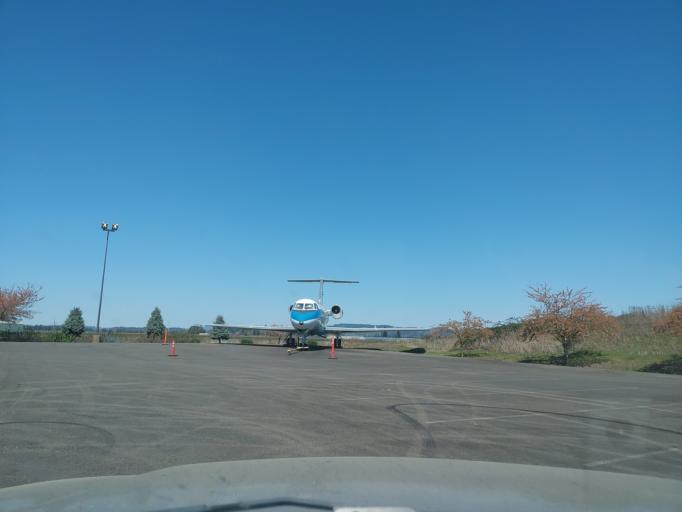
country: US
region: Oregon
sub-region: Yamhill County
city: Lafayette
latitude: 45.2055
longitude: -123.1412
